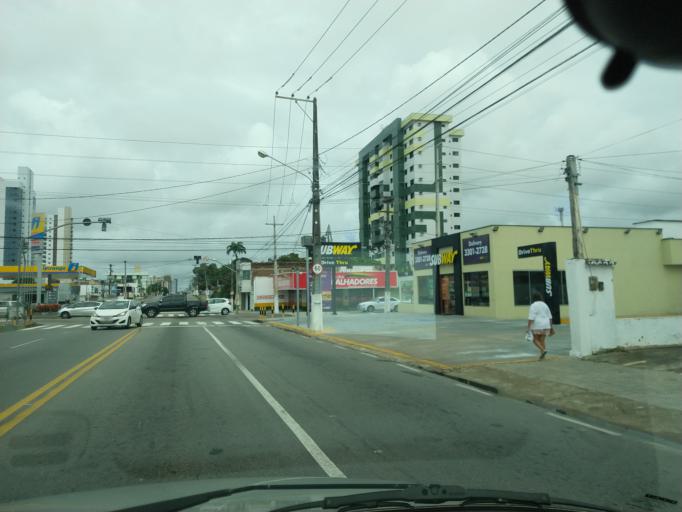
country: BR
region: Rio Grande do Norte
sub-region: Natal
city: Natal
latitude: -5.8169
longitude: -35.2177
